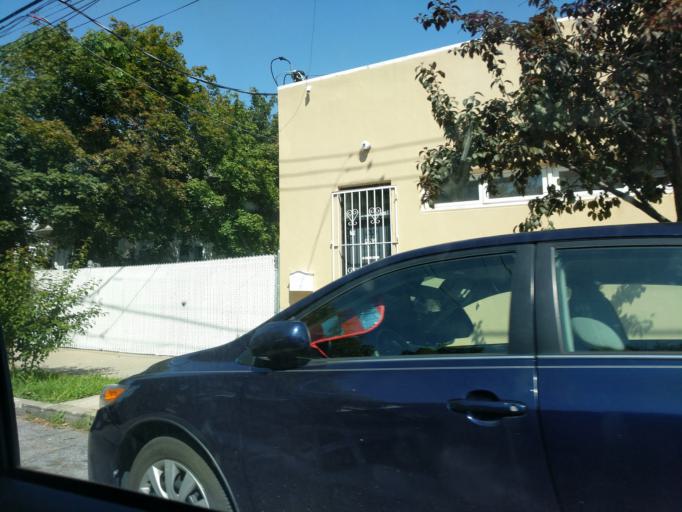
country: US
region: New Jersey
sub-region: Hudson County
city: Bayonne
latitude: 40.6324
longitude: -74.1186
